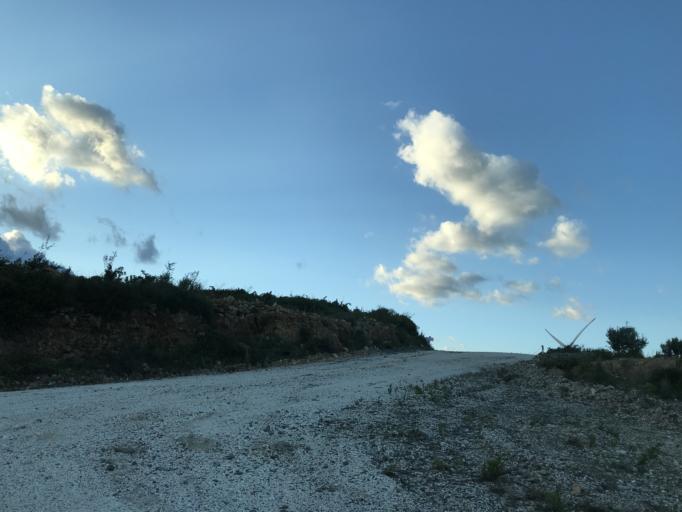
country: TR
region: Hatay
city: Buyukcat
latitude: 36.1001
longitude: 36.0431
